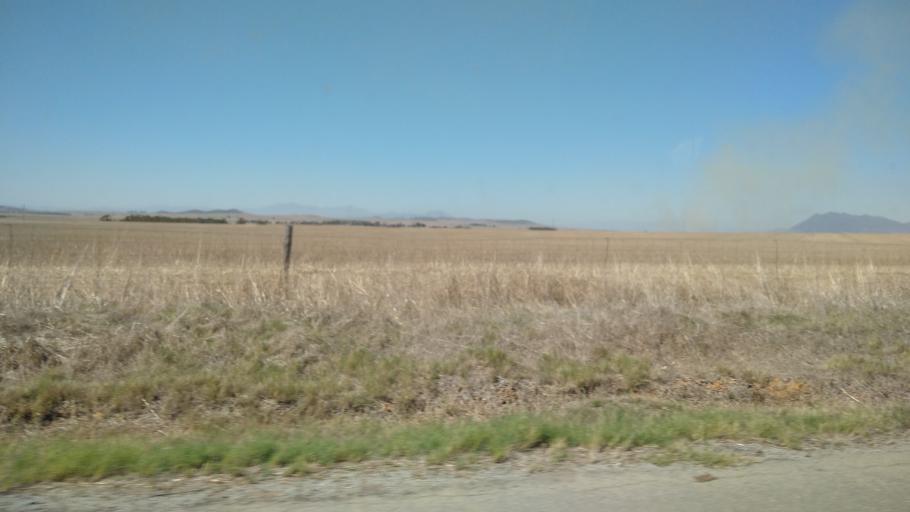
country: ZA
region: Western Cape
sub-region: West Coast District Municipality
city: Moorreesburg
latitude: -33.2899
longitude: 18.6082
